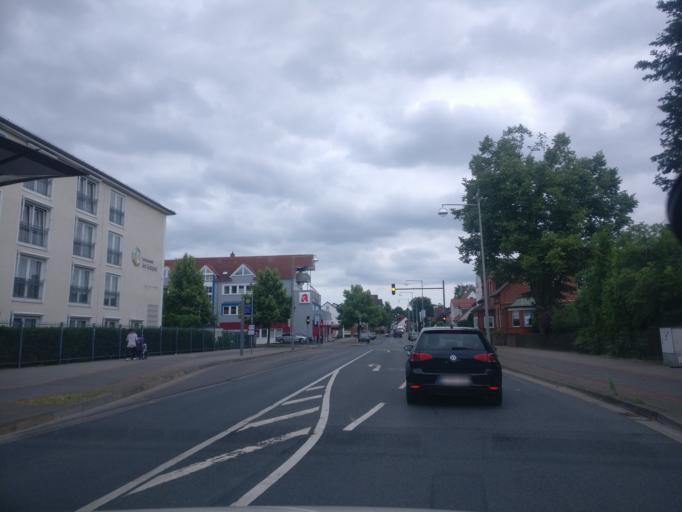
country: DE
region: Lower Saxony
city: Laatzen
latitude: 52.3447
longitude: 9.8271
